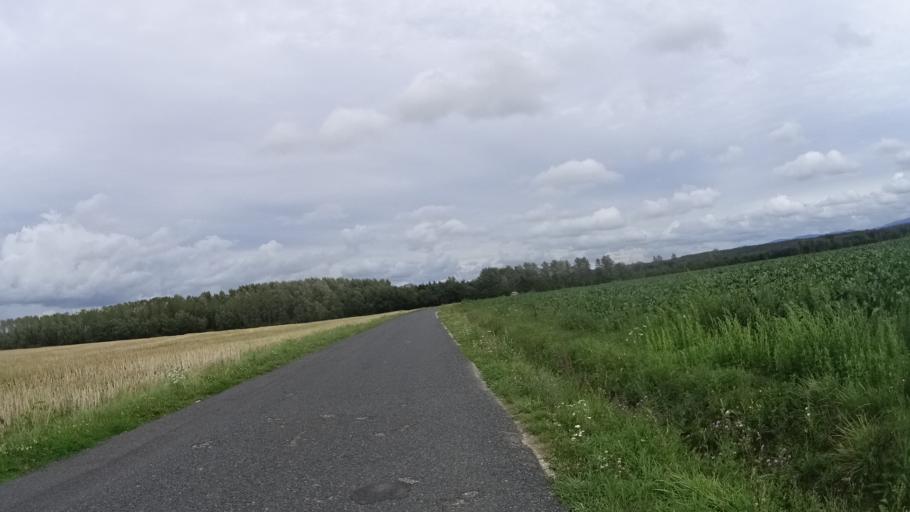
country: FR
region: Lorraine
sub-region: Departement de la Moselle
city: Sarrebourg
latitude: 48.6965
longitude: 7.0597
